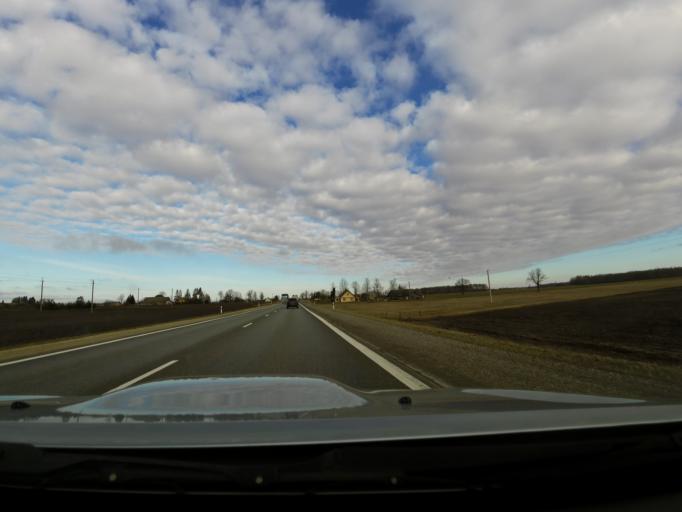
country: LT
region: Siauliu apskritis
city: Pakruojis
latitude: 55.7722
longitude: 24.0592
